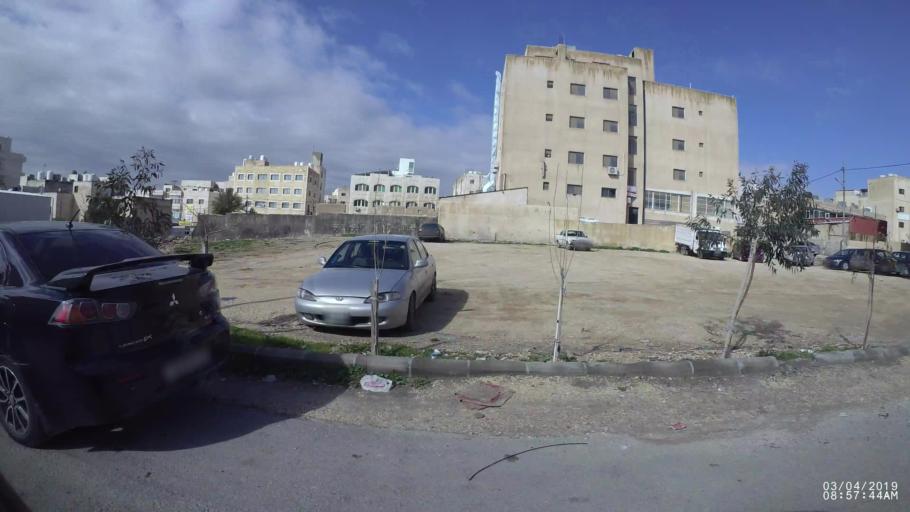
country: JO
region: Amman
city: Wadi as Sir
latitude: 31.9527
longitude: 35.8413
